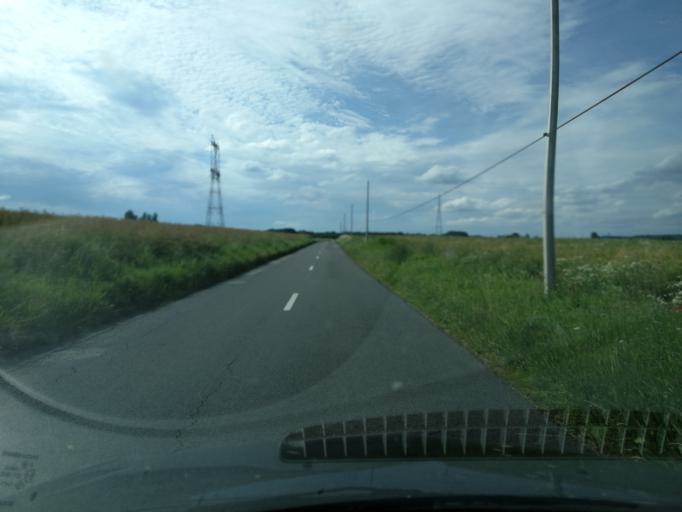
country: FR
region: Ile-de-France
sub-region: Departement de l'Essonne
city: Vaugrigneuse
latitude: 48.6108
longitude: 2.1313
